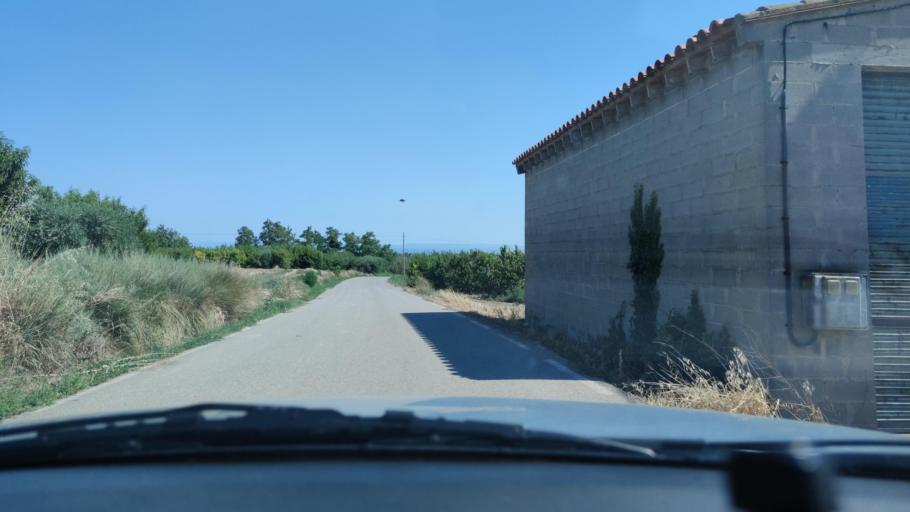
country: ES
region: Catalonia
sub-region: Provincia de Lleida
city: Torrefarrera
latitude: 41.6883
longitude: 0.6243
